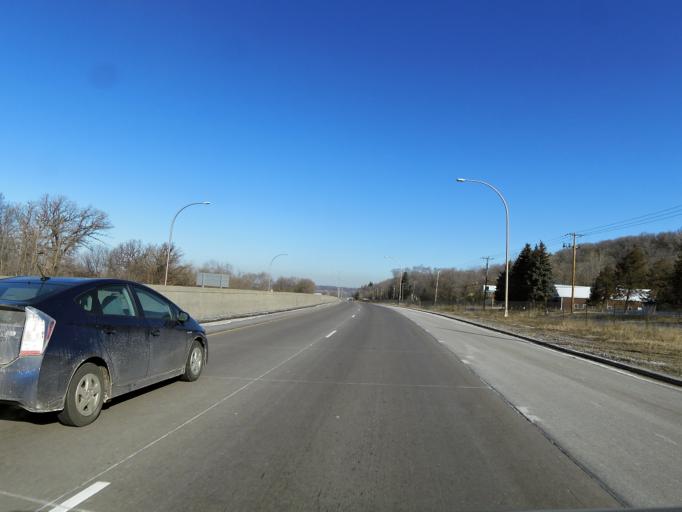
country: US
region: Minnesota
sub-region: Dakota County
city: South Saint Paul
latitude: 44.9024
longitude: -93.0102
